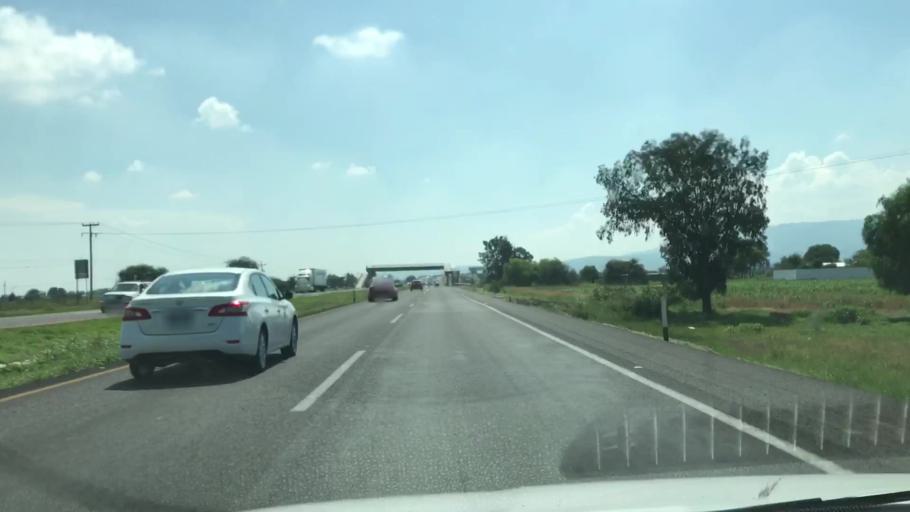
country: MX
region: Guanajuato
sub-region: Penjamo
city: Estacion Corralejo
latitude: 20.4481
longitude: -101.6300
